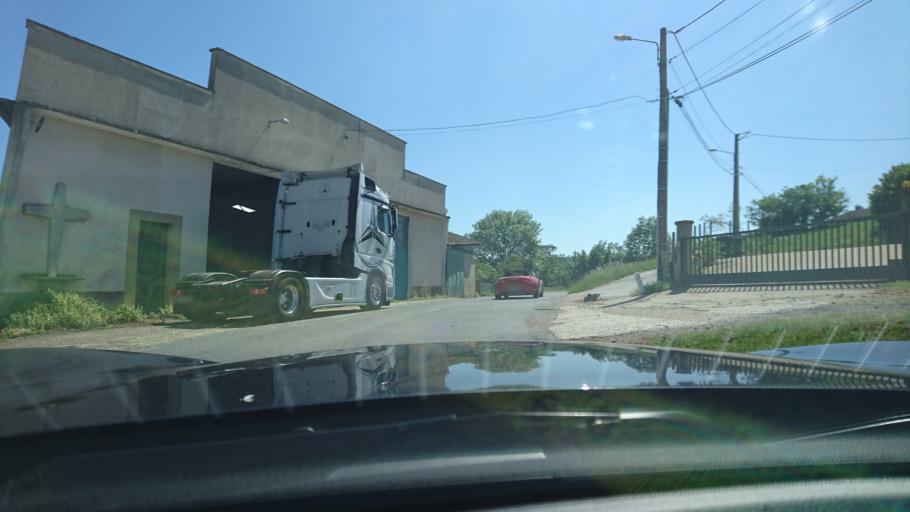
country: FR
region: Rhone-Alpes
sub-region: Departement de la Loire
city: Saint-Just-la-Pendue
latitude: 45.8799
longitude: 4.2811
